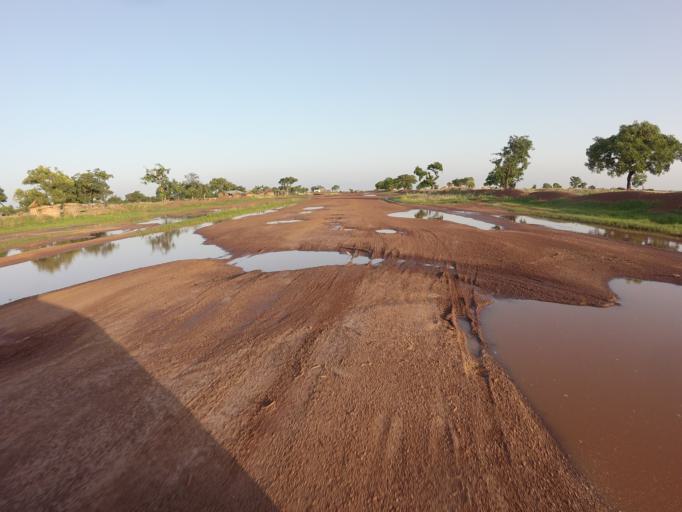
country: TG
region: Savanes
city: Sansanne-Mango
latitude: 10.2310
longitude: -0.0723
